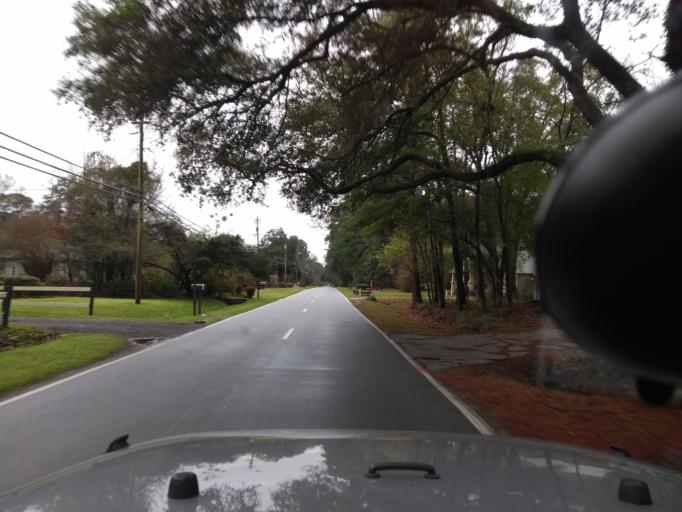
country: US
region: Georgia
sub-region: Chatham County
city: Savannah
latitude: 32.0333
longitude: -81.1593
